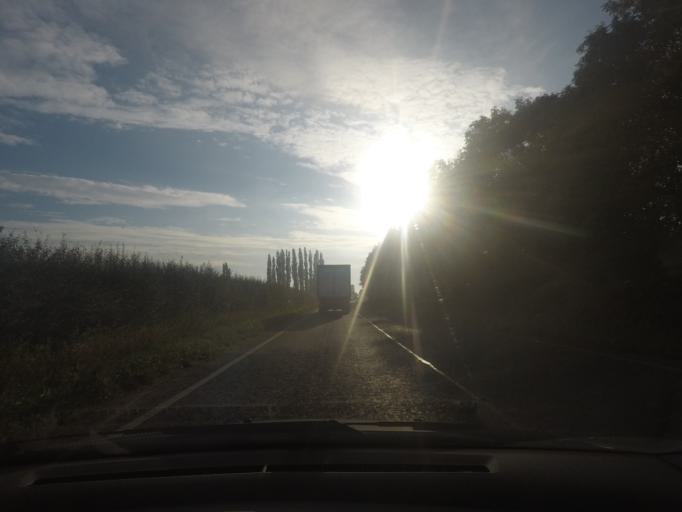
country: GB
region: England
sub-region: East Riding of Yorkshire
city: Hayton
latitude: 53.8940
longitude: -0.7402
